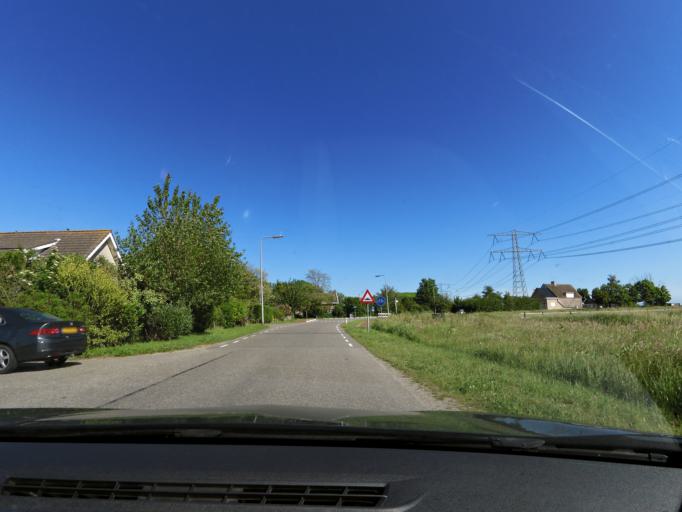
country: NL
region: South Holland
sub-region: Gemeente Brielle
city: Brielle
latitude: 51.8771
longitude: 4.1750
